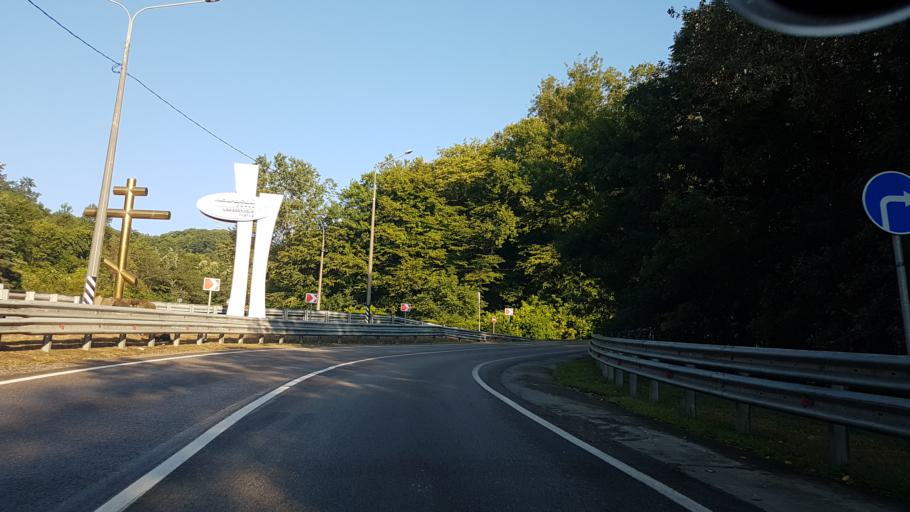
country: RU
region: Krasnodarskiy
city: Dagomys
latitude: 43.6445
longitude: 39.6967
